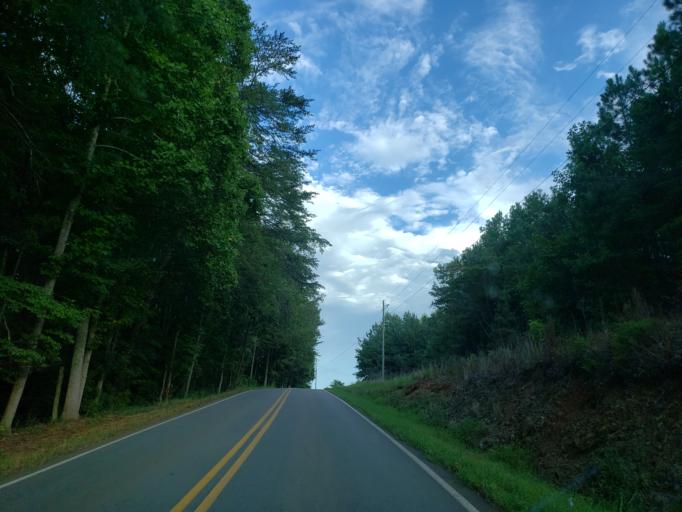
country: US
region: Georgia
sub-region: Cherokee County
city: Ball Ground
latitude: 34.3311
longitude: -84.4369
